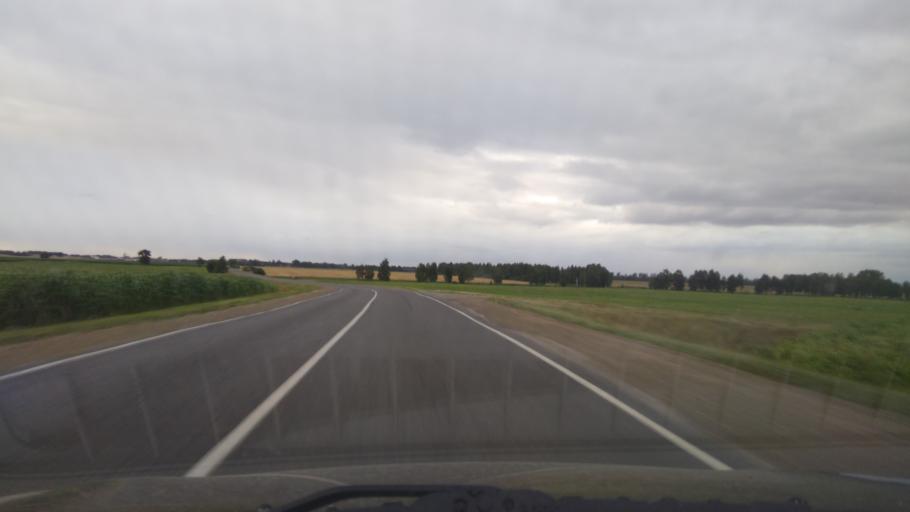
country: BY
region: Brest
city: Byaroza
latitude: 52.4343
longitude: 24.9803
